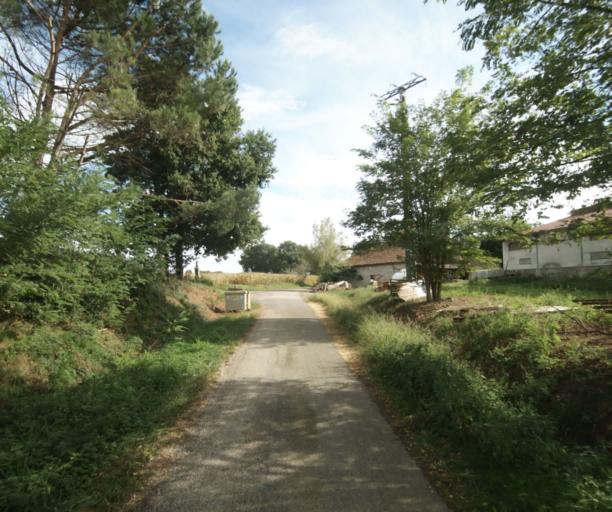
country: FR
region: Midi-Pyrenees
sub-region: Departement du Gers
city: Le Houga
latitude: 43.8764
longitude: -0.1691
